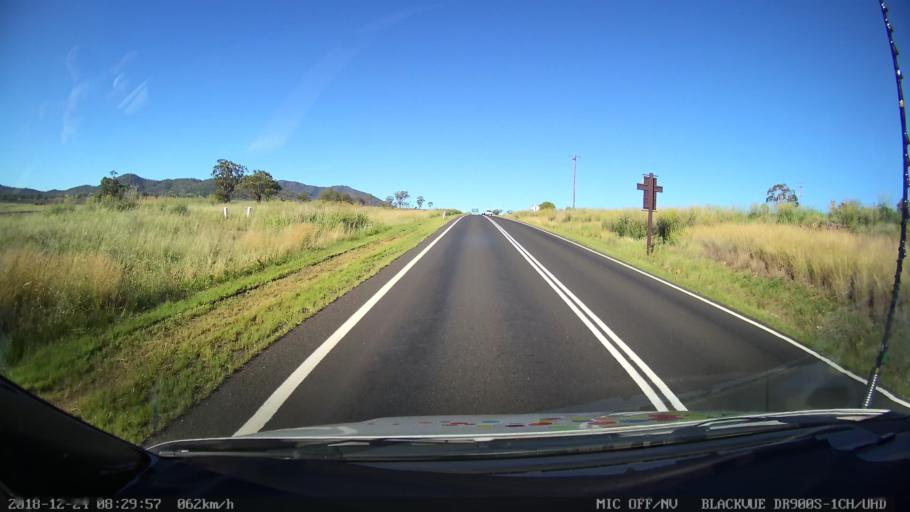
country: AU
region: New South Wales
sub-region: Tamworth Municipality
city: Phillip
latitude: -31.2653
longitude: 150.7298
